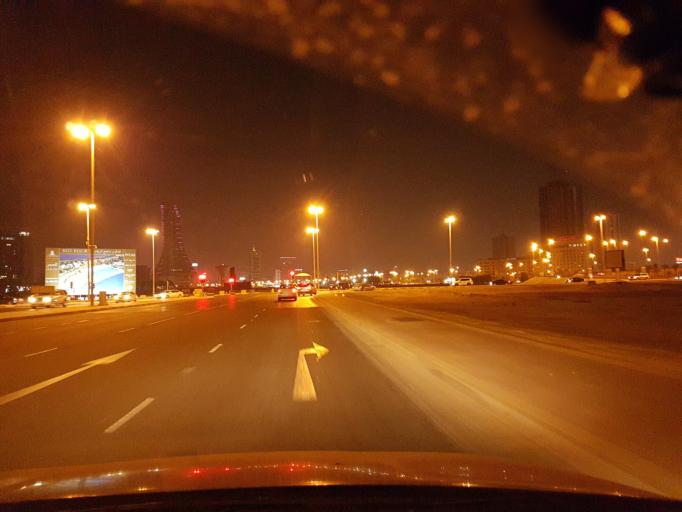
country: BH
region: Manama
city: Jidd Hafs
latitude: 26.2349
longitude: 50.5595
